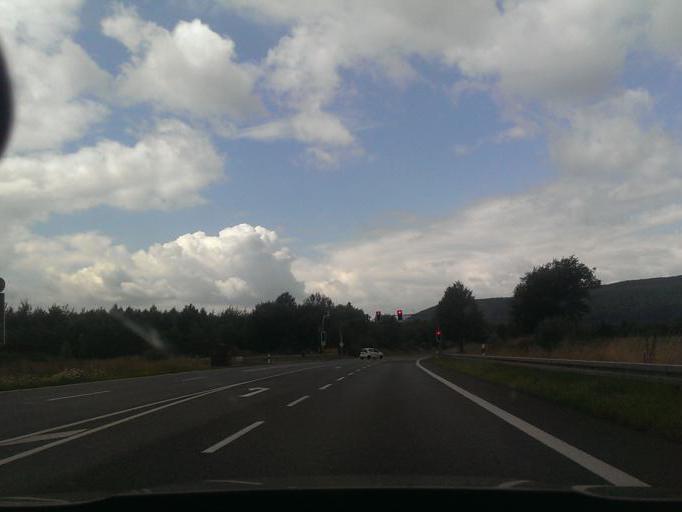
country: DE
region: Lower Saxony
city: Bevern
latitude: 51.8399
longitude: 9.4796
